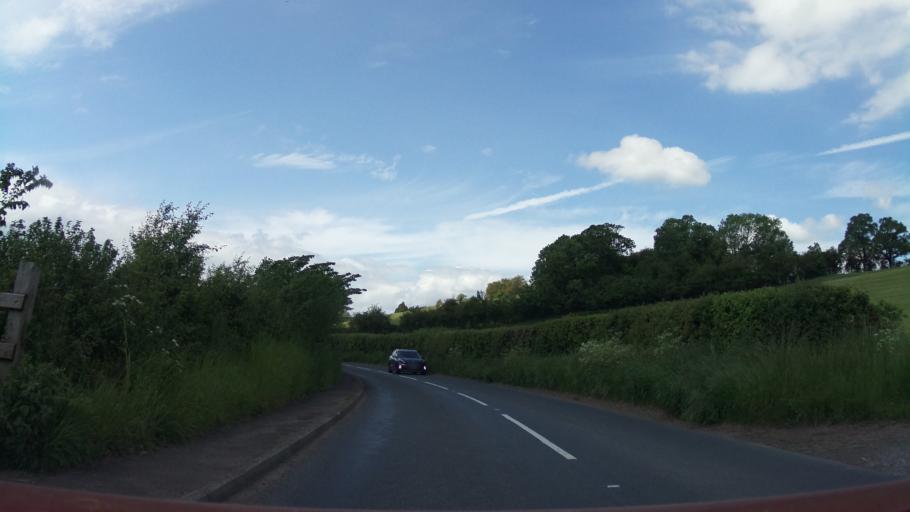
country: GB
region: Wales
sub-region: Monmouthshire
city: Monmouth
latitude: 51.8203
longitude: -2.7365
